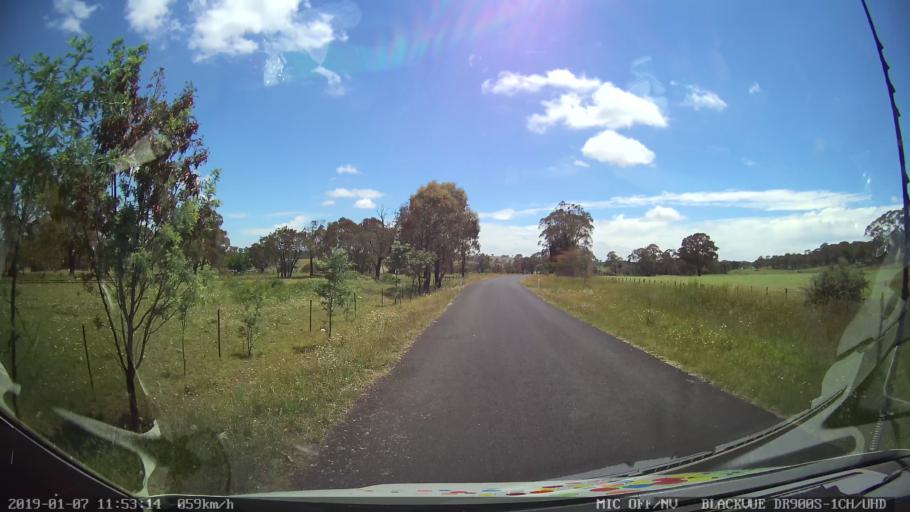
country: AU
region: New South Wales
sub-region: Guyra
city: Guyra
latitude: -30.3059
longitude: 151.6562
